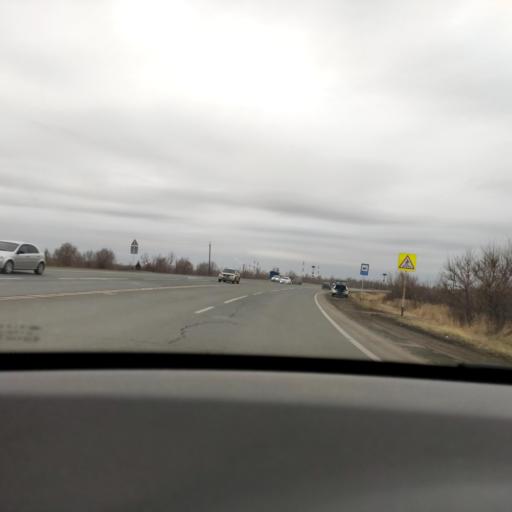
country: RU
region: Samara
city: Novokuybyshevsk
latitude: 53.0712
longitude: 50.0283
